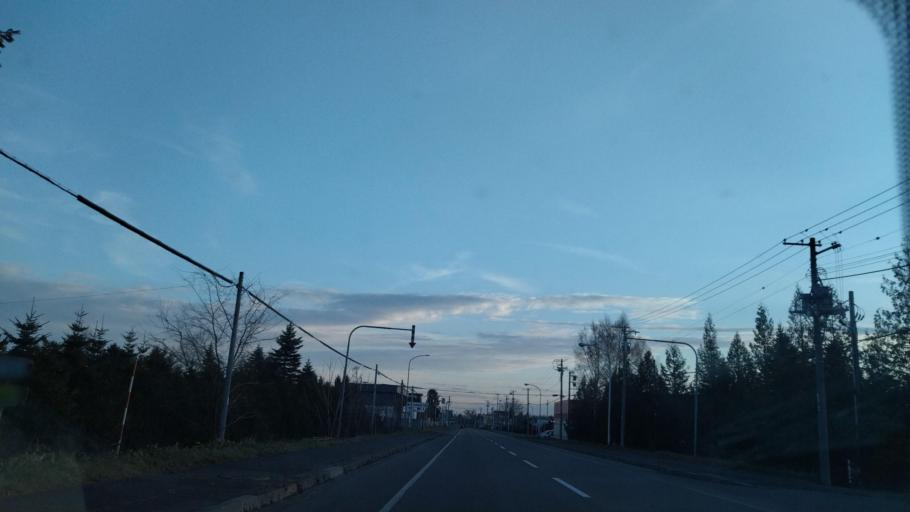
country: JP
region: Hokkaido
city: Otofuke
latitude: 42.9948
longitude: 143.2027
